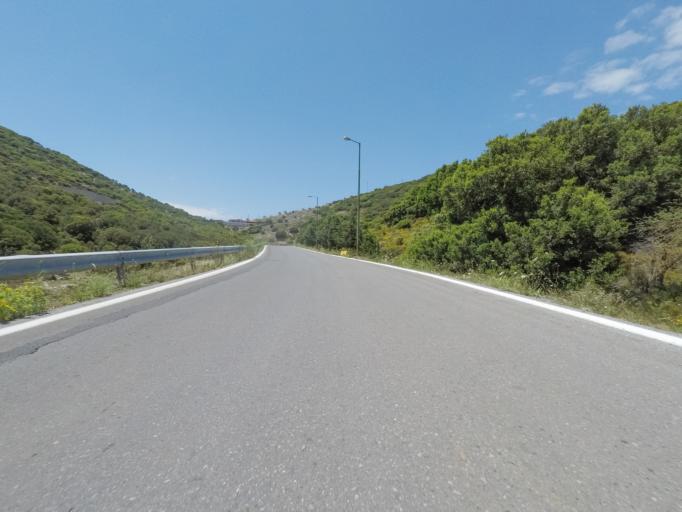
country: GR
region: Crete
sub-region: Nomos Irakleiou
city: Mokhos
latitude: 35.2012
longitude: 25.4596
